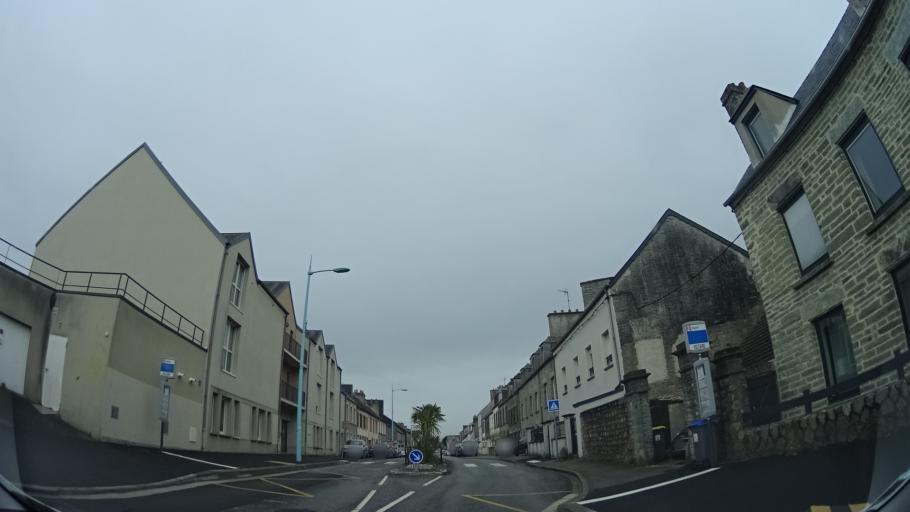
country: FR
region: Lower Normandy
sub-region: Departement de la Manche
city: Octeville
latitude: 49.6316
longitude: -1.6385
